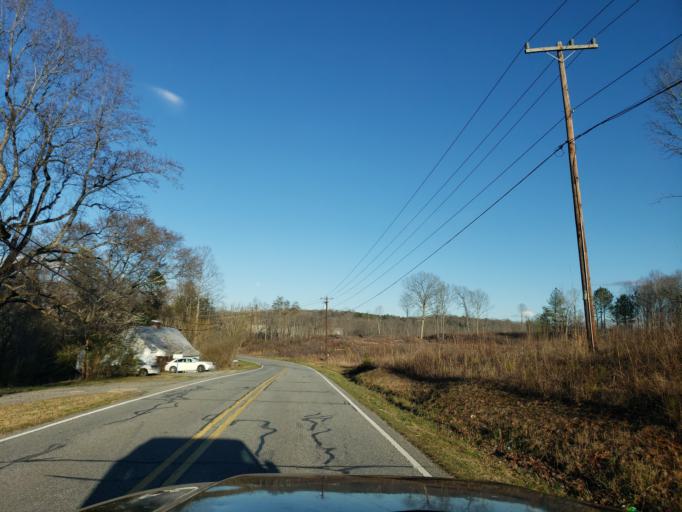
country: US
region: North Carolina
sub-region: Cleveland County
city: Shelby
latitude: 35.4103
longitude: -81.5679
